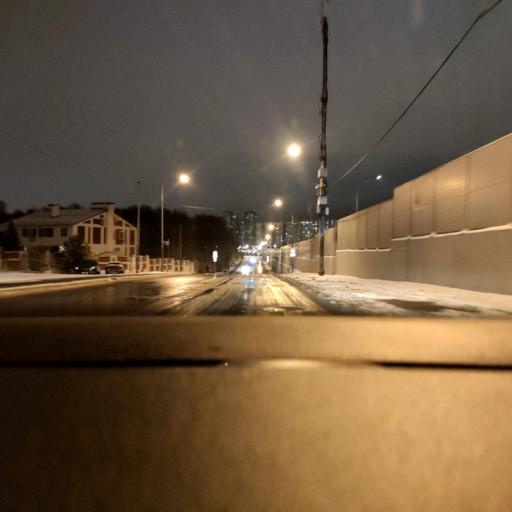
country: RU
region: Moskovskaya
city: Pavshino
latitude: 55.8615
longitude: 37.3613
